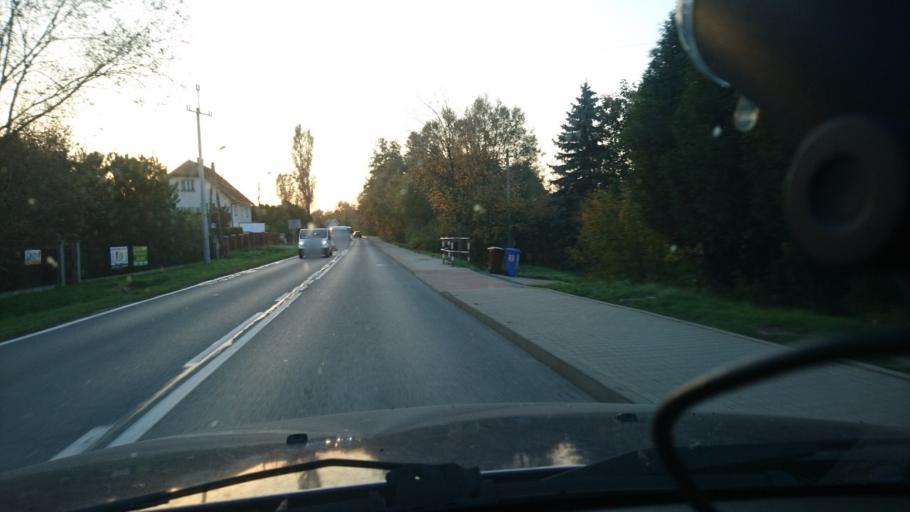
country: PL
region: Silesian Voivodeship
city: Janowice
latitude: 49.8521
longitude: 19.1057
